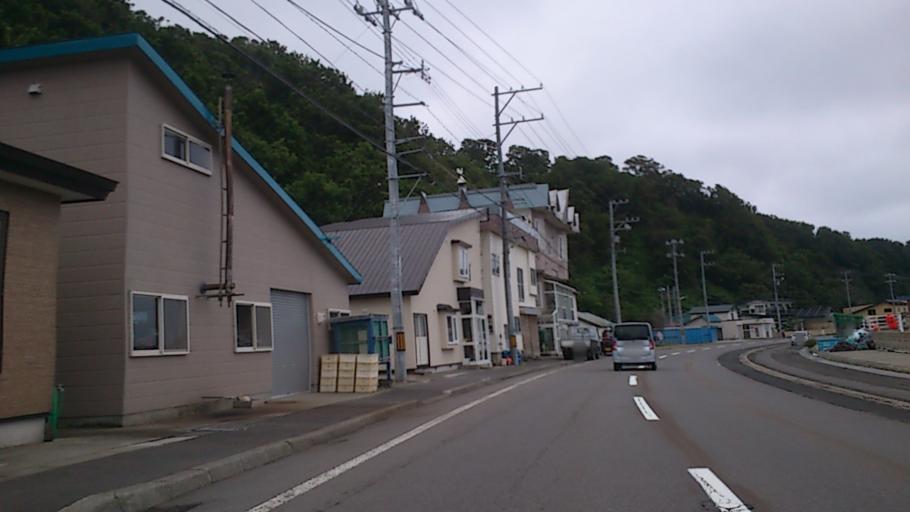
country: JP
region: Hokkaido
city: Iwanai
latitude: 42.7308
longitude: 140.0866
